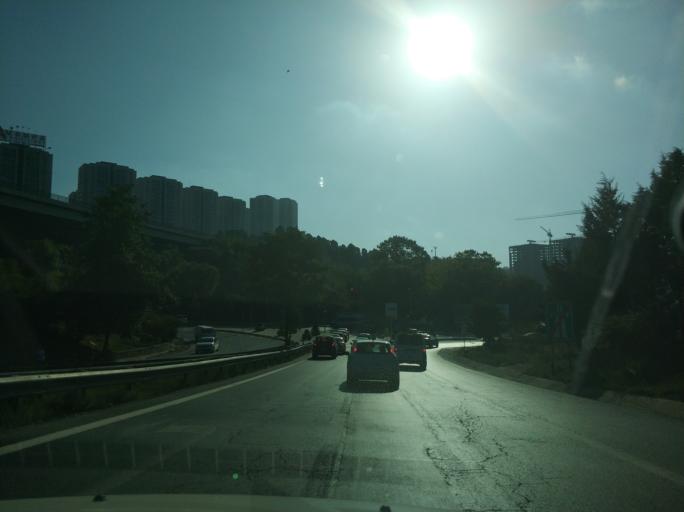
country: TR
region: Istanbul
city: Sultangazi
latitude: 41.0916
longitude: 28.9076
